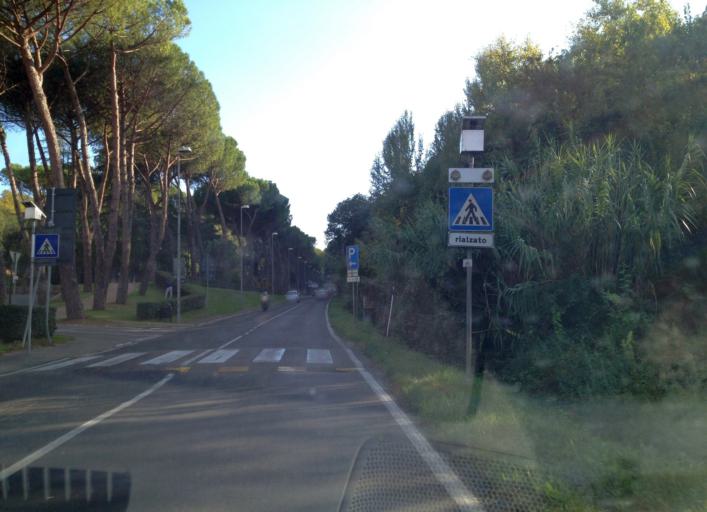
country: IT
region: Tuscany
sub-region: Provincia di Siena
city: Poggibonsi
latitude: 43.4653
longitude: 11.1449
